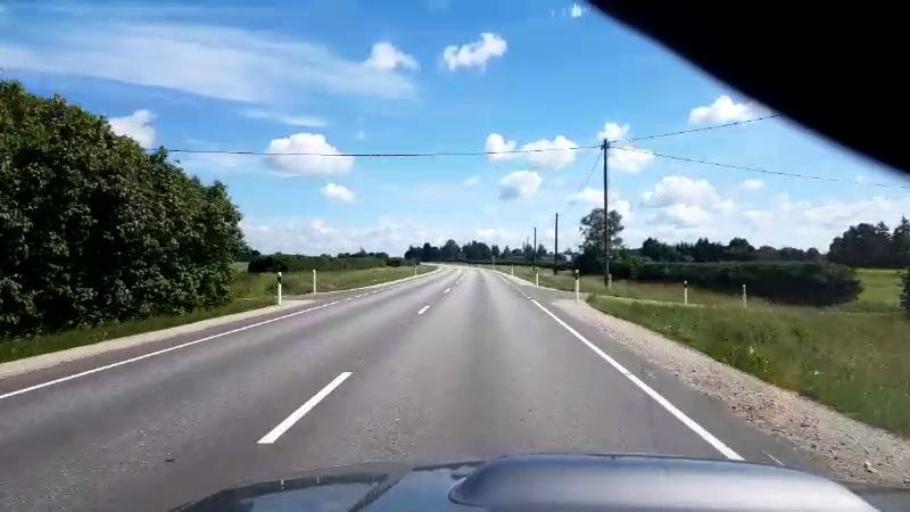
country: EE
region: Jaervamaa
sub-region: Jaerva-Jaani vald
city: Jarva-Jaani
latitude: 59.1060
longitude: 25.7156
